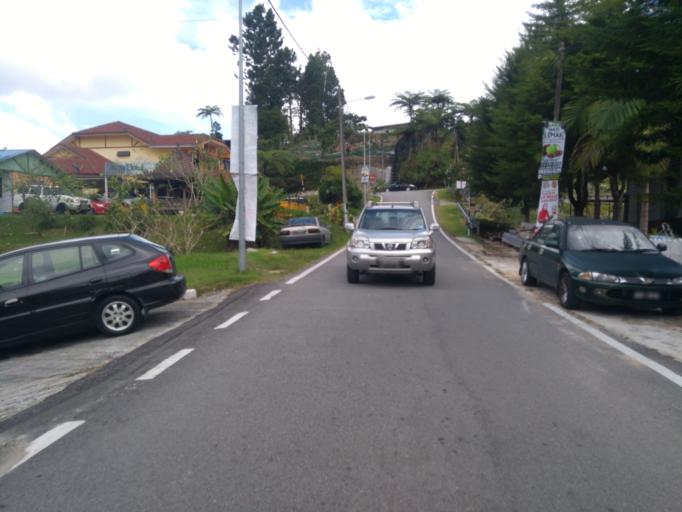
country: MY
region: Pahang
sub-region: Cameron Highlands
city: Tanah Rata
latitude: 4.4785
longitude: 101.3810
